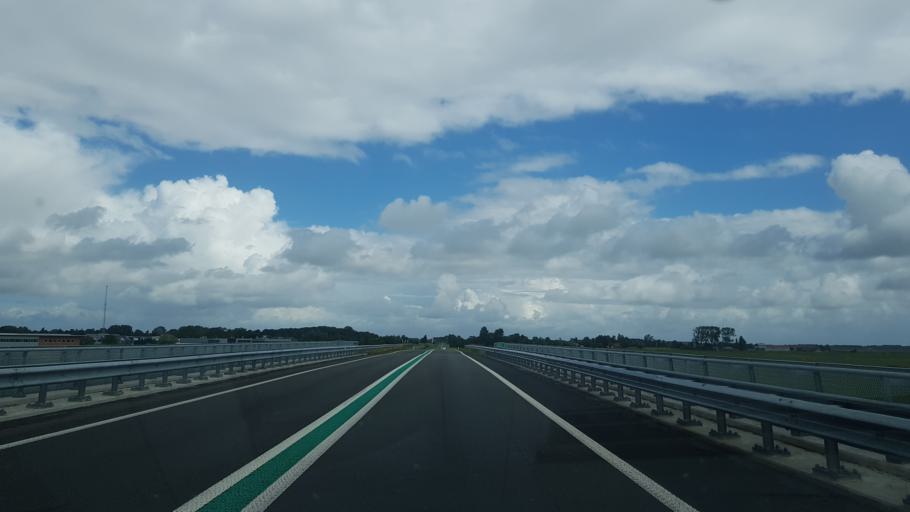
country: NL
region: Friesland
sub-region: Gemeente Dantumadiel
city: Walterswald
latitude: 53.3171
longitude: 6.0216
